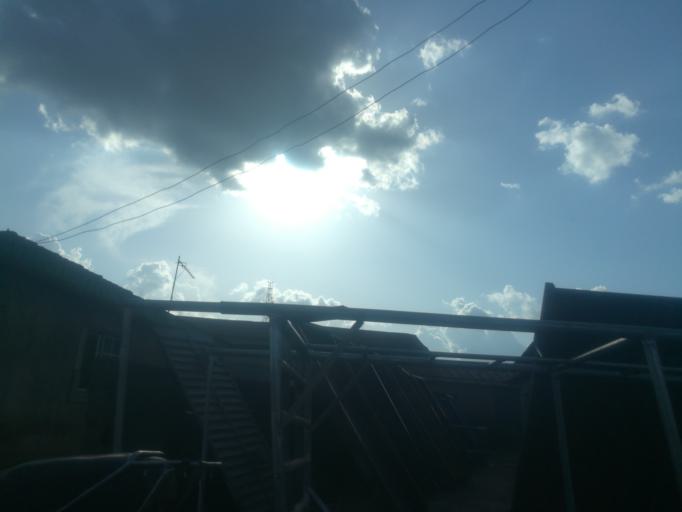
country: NG
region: Oyo
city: Lalupon
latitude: 7.4407
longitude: 3.9812
